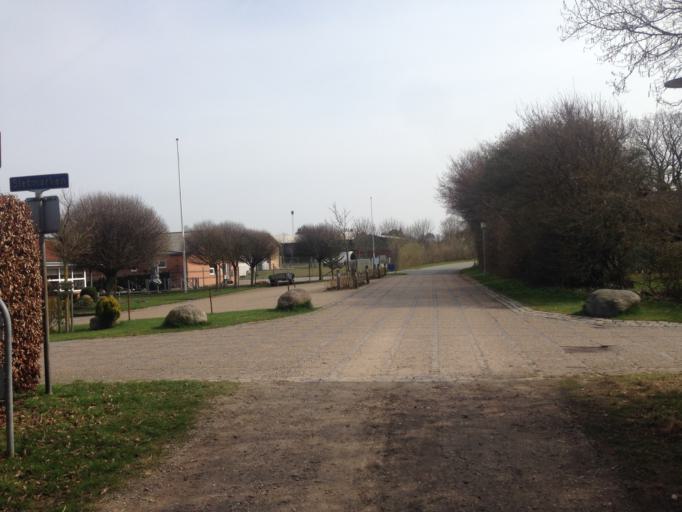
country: DK
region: South Denmark
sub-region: Sonderborg Kommune
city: Broager
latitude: 54.8921
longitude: 9.6540
